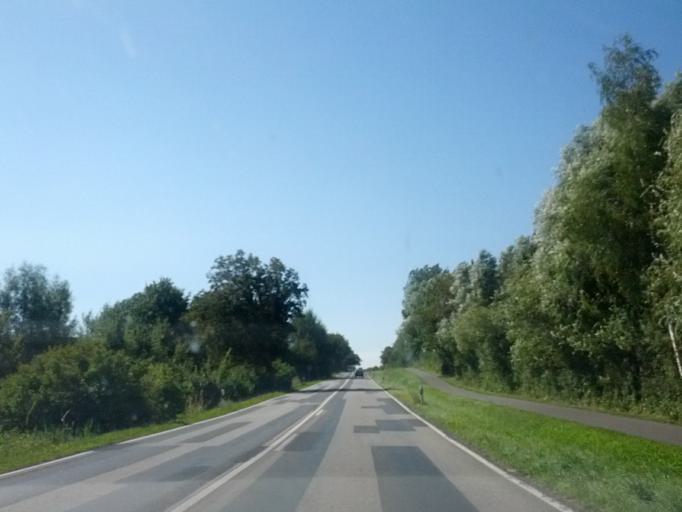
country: DE
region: Mecklenburg-Vorpommern
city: Sagard
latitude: 54.5024
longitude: 13.5283
